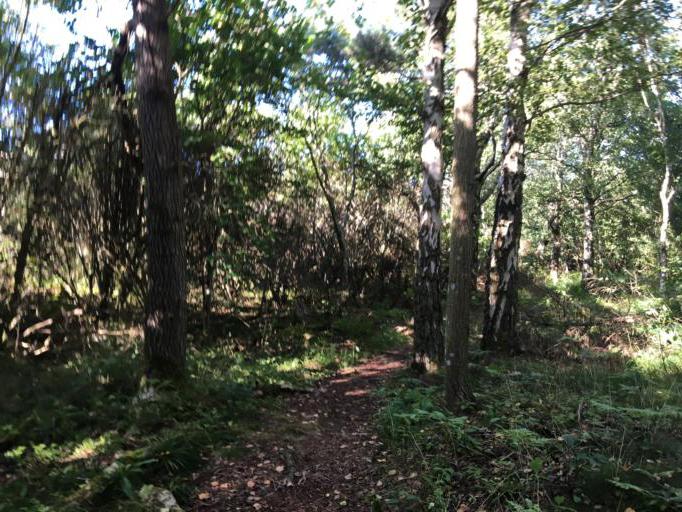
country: SE
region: Vaestra Goetaland
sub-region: Sotenas Kommun
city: Hunnebostrand
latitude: 58.4408
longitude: 11.2509
